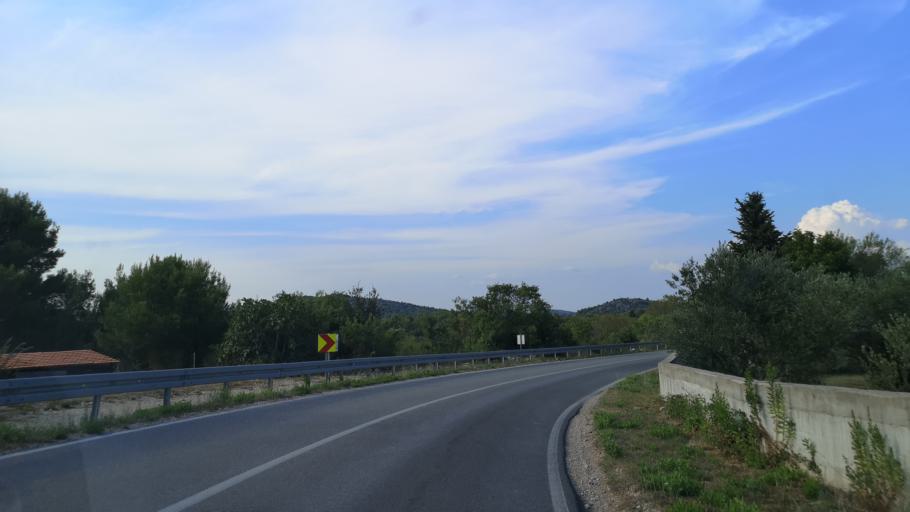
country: HR
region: Sibensko-Kniniska
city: Vodice
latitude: 43.7887
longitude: 15.7697
